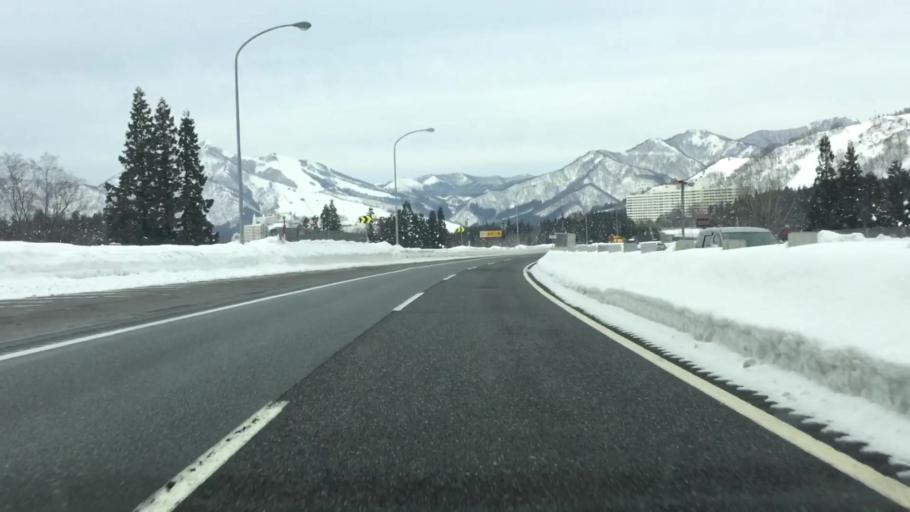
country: JP
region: Niigata
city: Shiozawa
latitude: 36.8964
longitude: 138.8452
